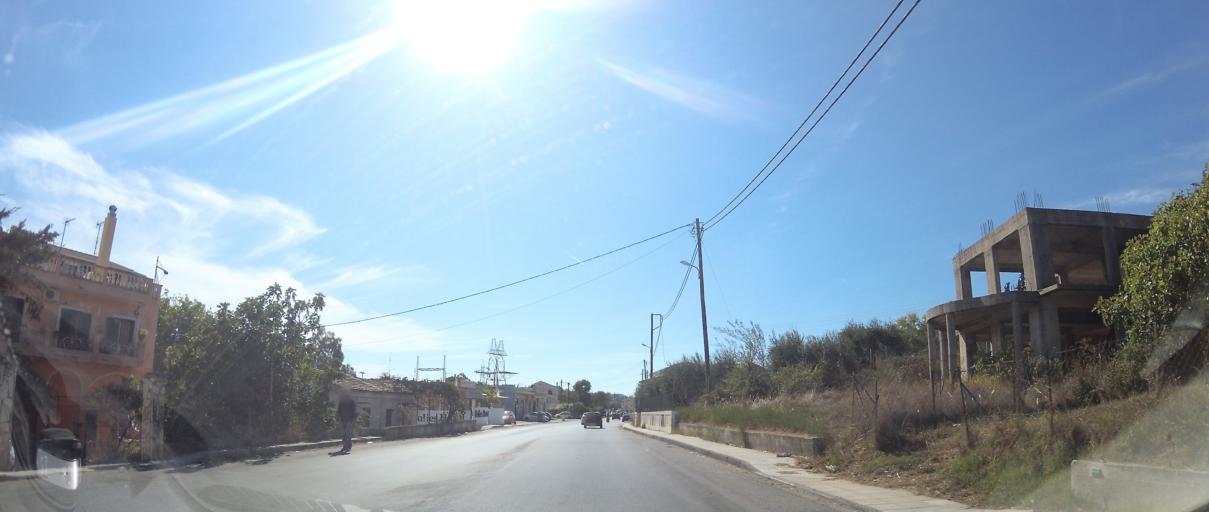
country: GR
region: Ionian Islands
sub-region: Nomos Kerkyras
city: Alepou
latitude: 39.6173
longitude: 19.8986
